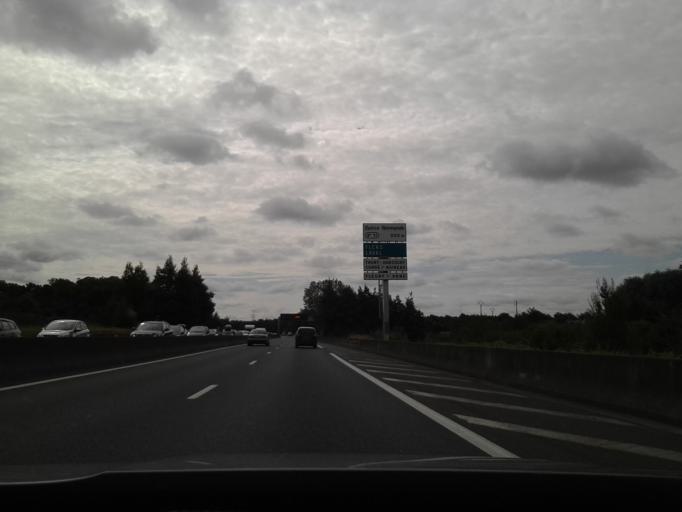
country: FR
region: Lower Normandy
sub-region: Departement du Calvados
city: Louvigny
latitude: 49.1392
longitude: -0.3961
